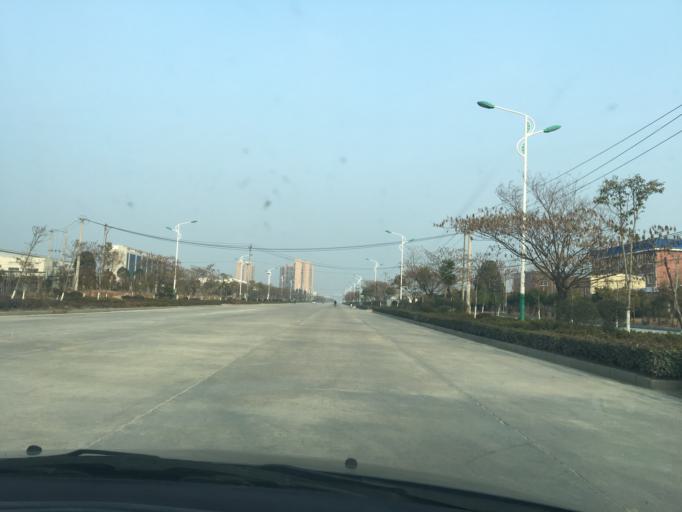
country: CN
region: Hubei
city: Nanhu
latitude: 31.1510
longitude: 114.9698
